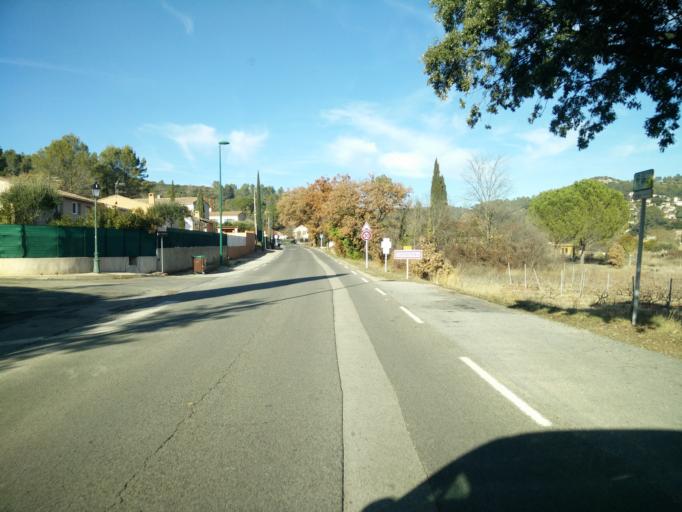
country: FR
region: Provence-Alpes-Cote d'Azur
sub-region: Departement du Var
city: Taradeau
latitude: 43.4518
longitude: 6.4240
